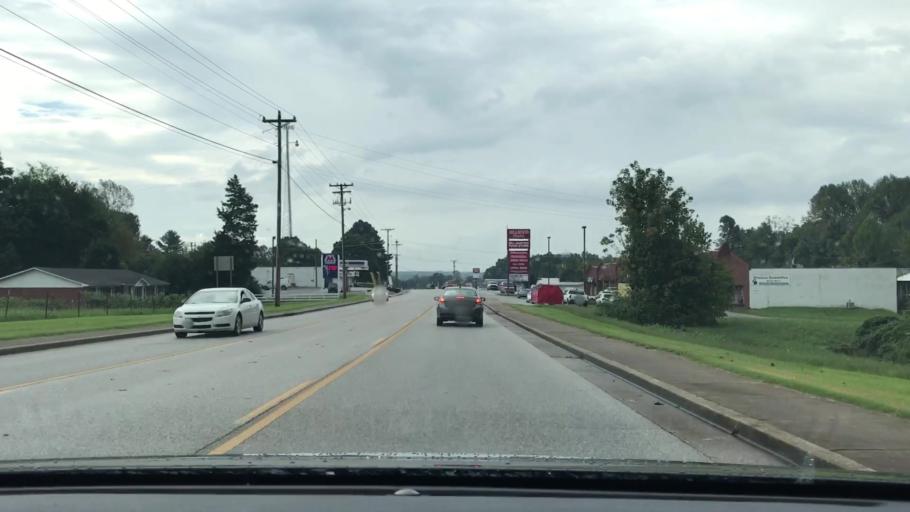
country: US
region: Tennessee
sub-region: Macon County
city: Red Boiling Springs
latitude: 36.5210
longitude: -85.8651
